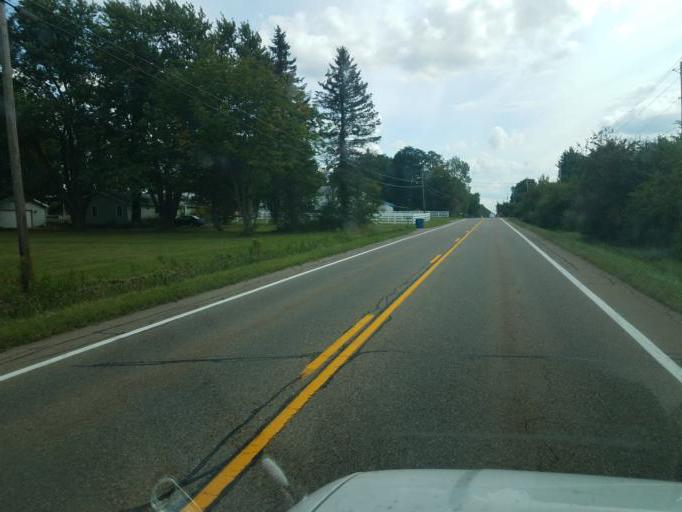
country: US
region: Ohio
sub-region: Stark County
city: Hartville
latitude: 40.9943
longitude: -81.2493
